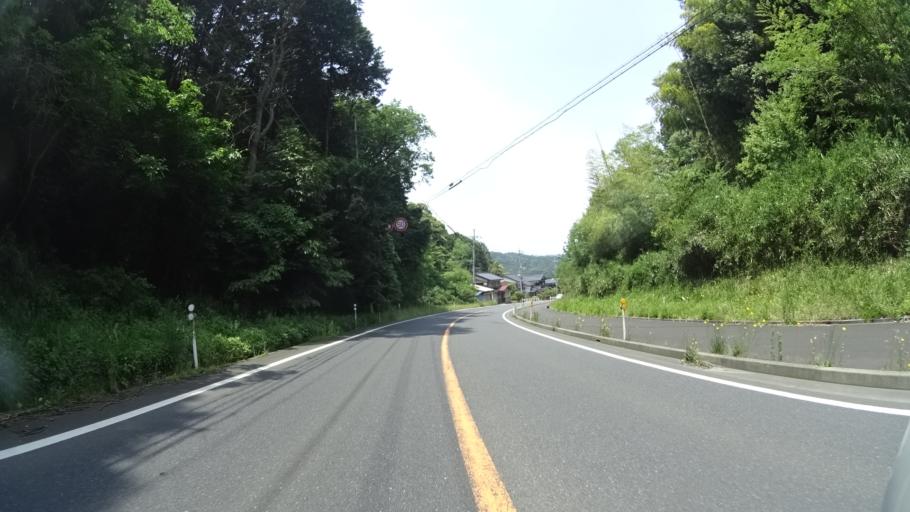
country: JP
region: Hyogo
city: Toyooka
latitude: 35.5897
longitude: 134.9352
